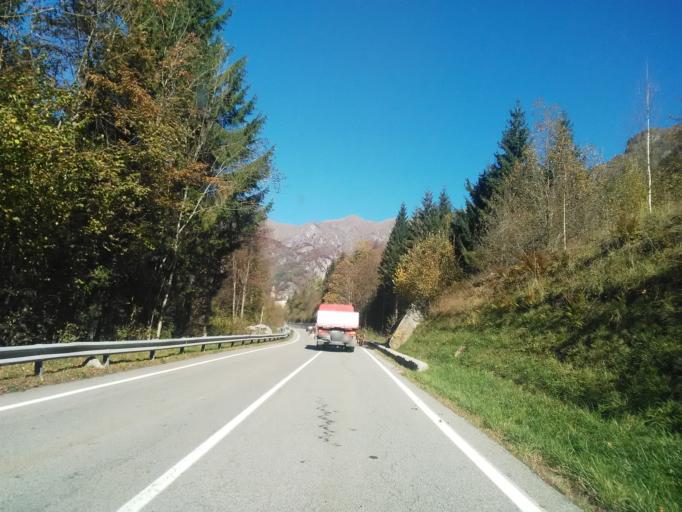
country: IT
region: Piedmont
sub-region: Provincia di Vercelli
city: Campertogno
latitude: 45.7889
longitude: 8.0395
